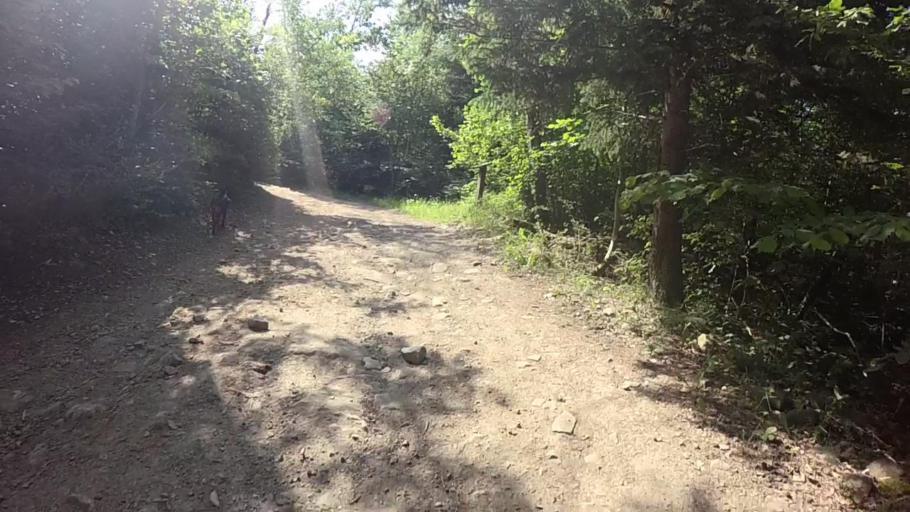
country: FR
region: Provence-Alpes-Cote d'Azur
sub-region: Departement des Alpes-de-Haute-Provence
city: Seyne-les-Alpes
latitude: 44.4054
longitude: 6.3530
